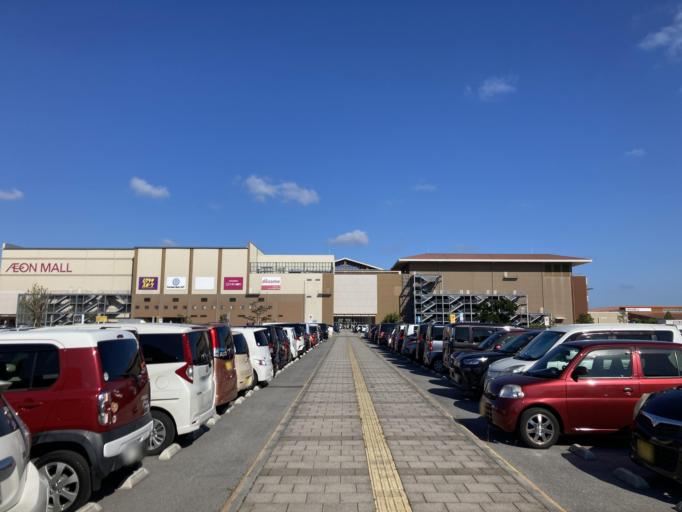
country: JP
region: Okinawa
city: Okinawa
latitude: 26.3121
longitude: 127.7966
